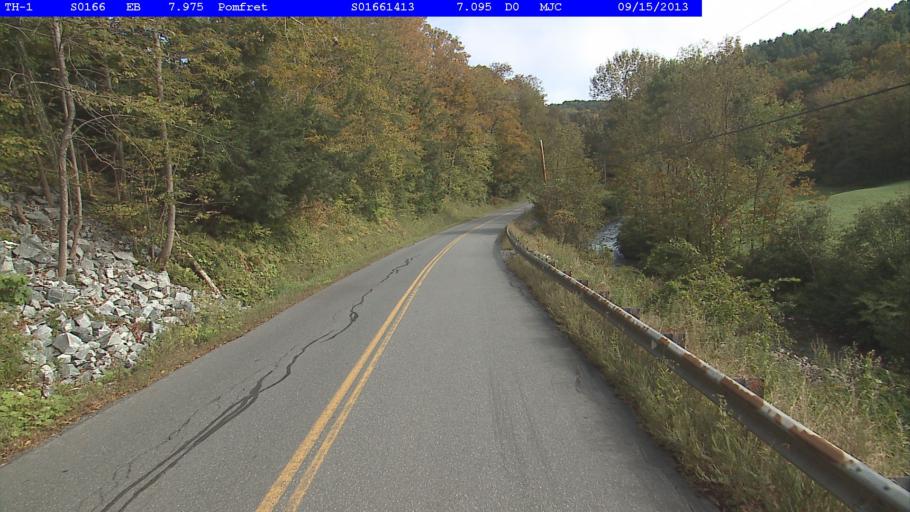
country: US
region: Vermont
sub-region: Windsor County
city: Woodstock
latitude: 43.7230
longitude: -72.4793
